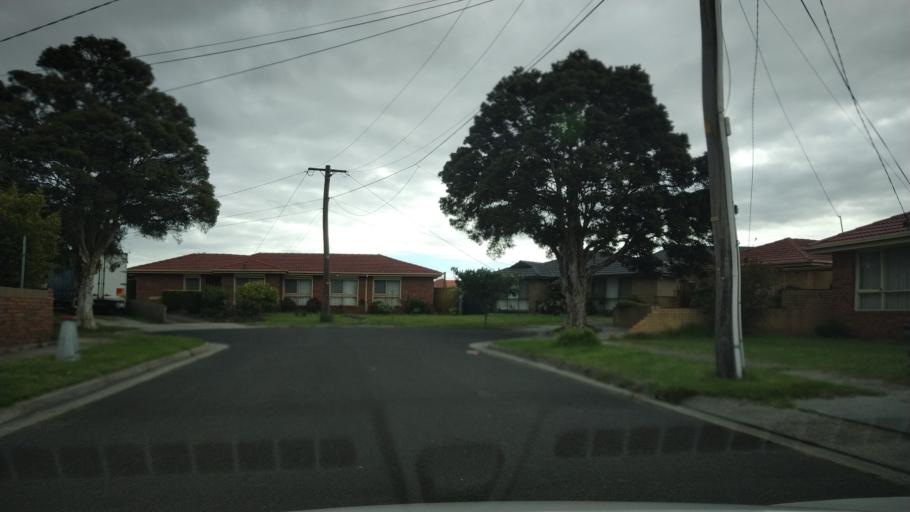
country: AU
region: Victoria
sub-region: Greater Dandenong
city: Springvale South
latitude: -37.9727
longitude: 145.1560
